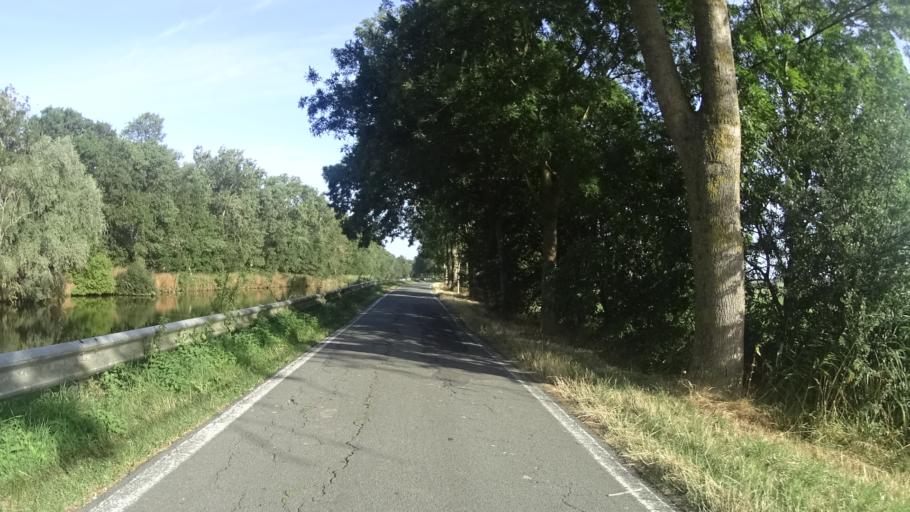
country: BE
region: Flanders
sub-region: Provincie West-Vlaanderen
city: Diksmuide
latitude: 50.9714
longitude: 2.8135
